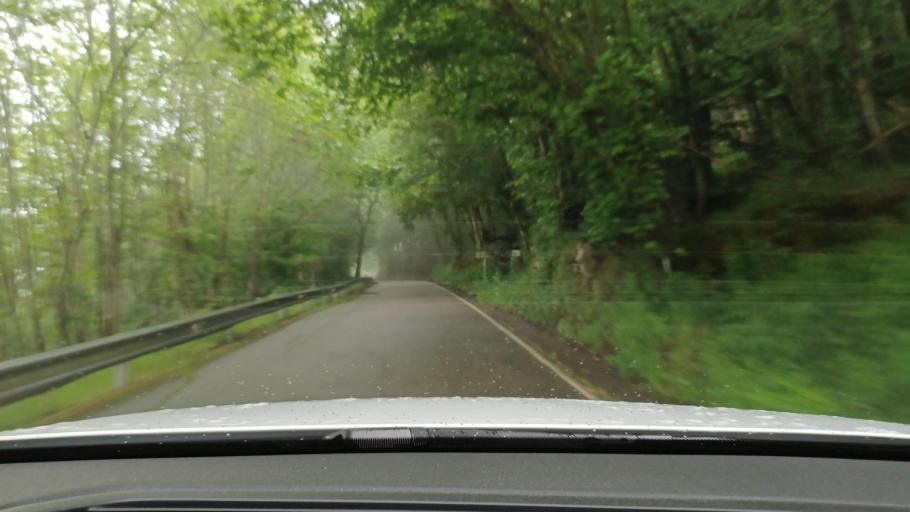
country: ES
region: Asturias
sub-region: Province of Asturias
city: Castandiello
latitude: 43.2999
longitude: -5.9483
